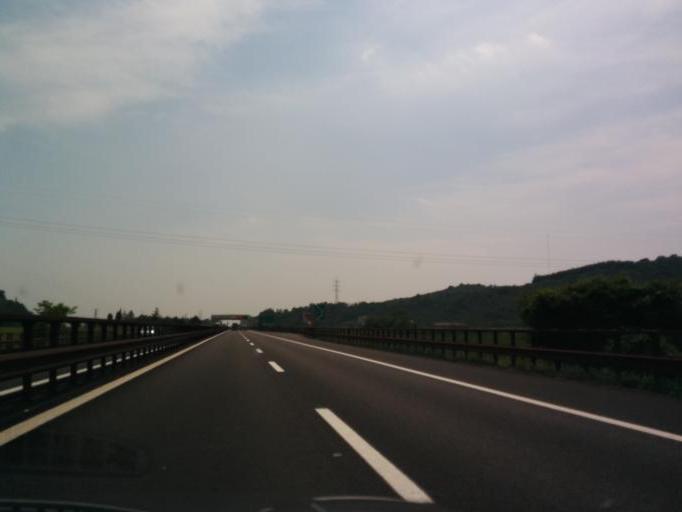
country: IT
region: Veneto
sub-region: Provincia di Verona
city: Rivoli Veronese
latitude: 45.5636
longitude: 10.8016
